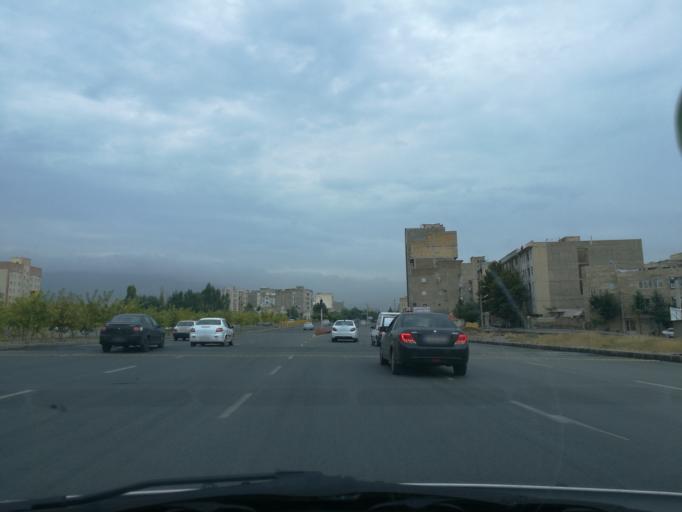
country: IR
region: Alborz
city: Karaj
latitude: 35.8620
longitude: 50.9359
